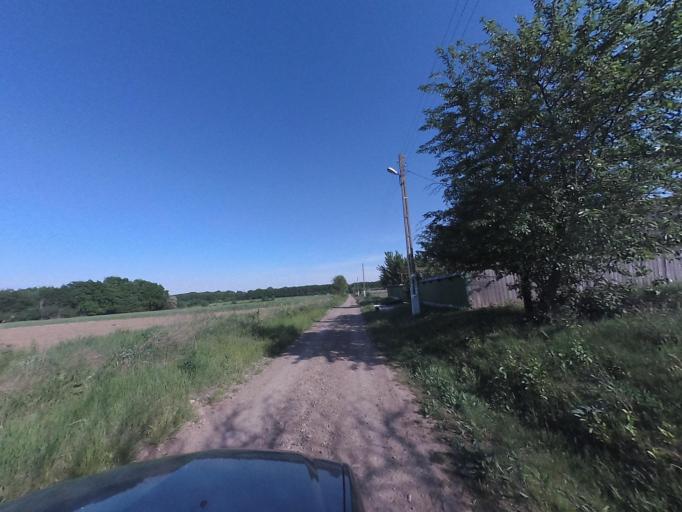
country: RO
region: Neamt
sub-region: Comuna Dulcesti
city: Dulcesti
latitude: 47.0002
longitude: 26.7782
